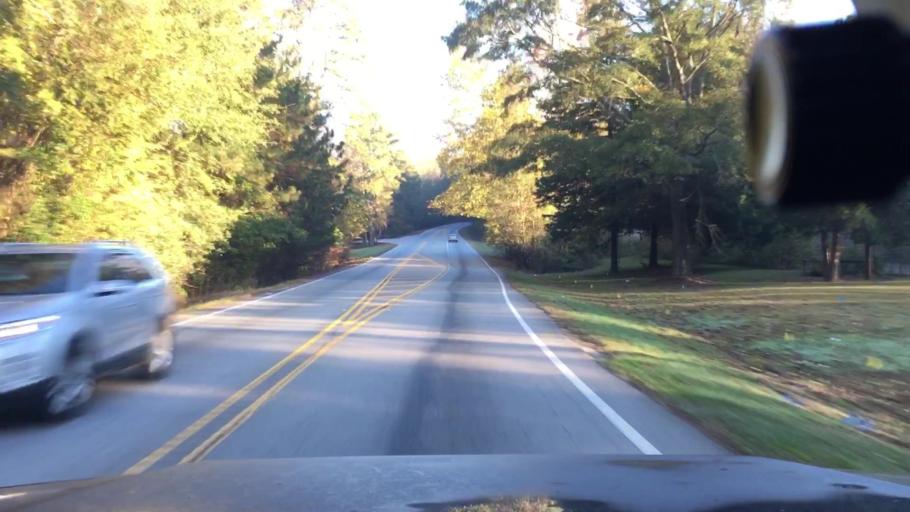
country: US
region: Georgia
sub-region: Fulton County
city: Palmetto
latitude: 33.4361
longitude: -84.6917
